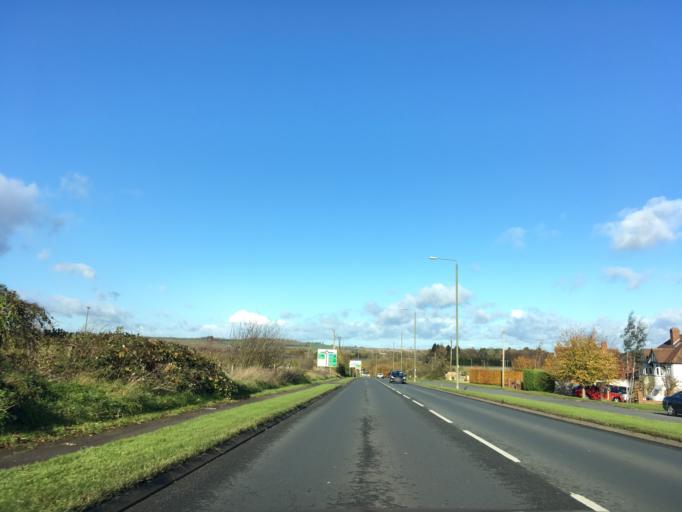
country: GB
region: England
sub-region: Worcestershire
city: Evesham
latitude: 52.1109
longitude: -1.9443
